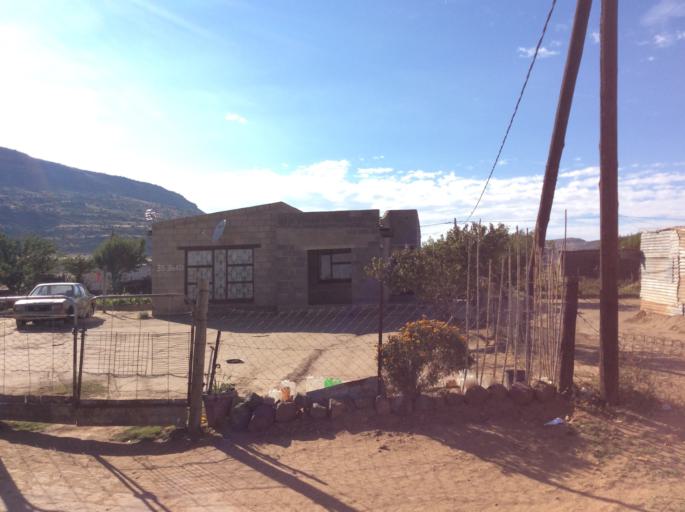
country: LS
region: Mafeteng
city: Mafeteng
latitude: -29.7115
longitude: 27.0152
